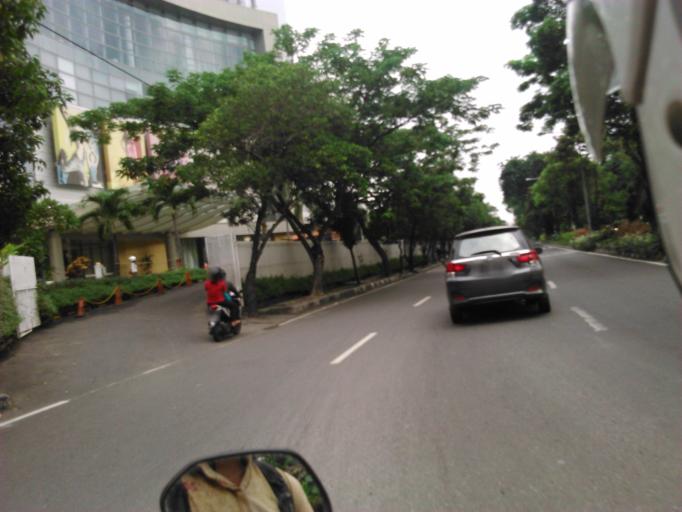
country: ID
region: East Java
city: Pacarkeling
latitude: -7.2621
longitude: 112.7513
